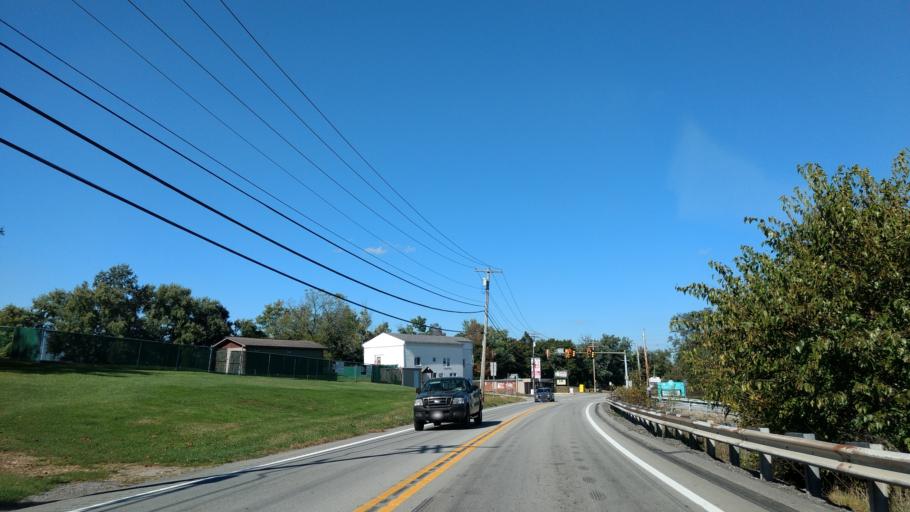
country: US
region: Pennsylvania
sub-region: Washington County
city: Wickerham Manor-Fisher
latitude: 40.1811
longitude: -79.9161
